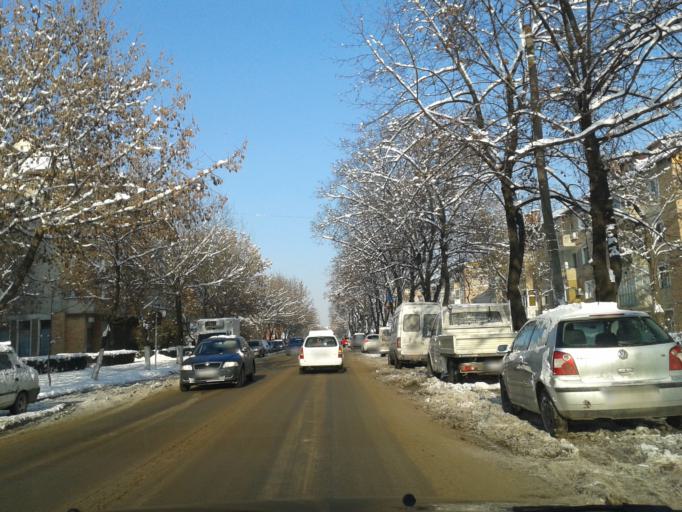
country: RO
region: Hunedoara
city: Hunedoara
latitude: 45.7557
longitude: 22.9011
